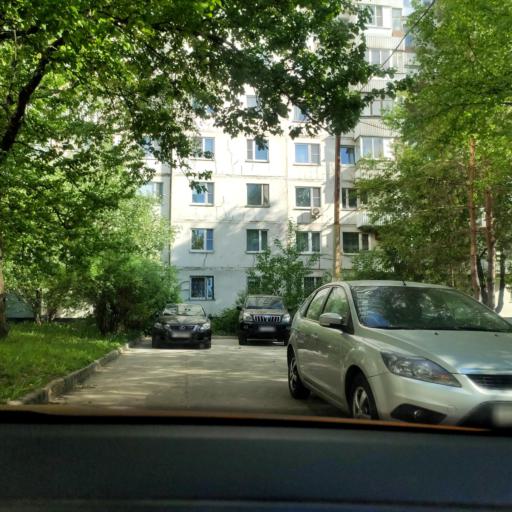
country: RU
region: Moscow
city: Nagornyy
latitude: 55.6613
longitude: 37.6477
